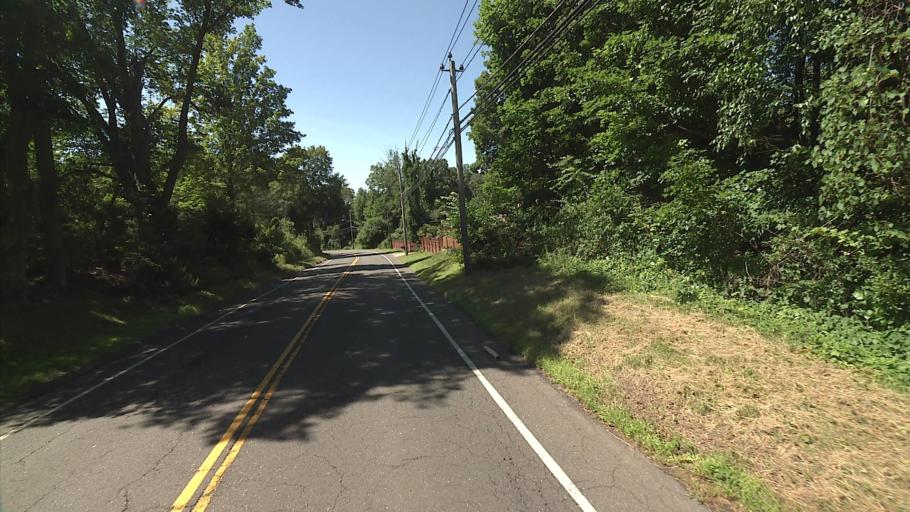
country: US
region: Connecticut
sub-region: Hartford County
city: Weatogue
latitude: 41.7862
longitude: -72.8176
